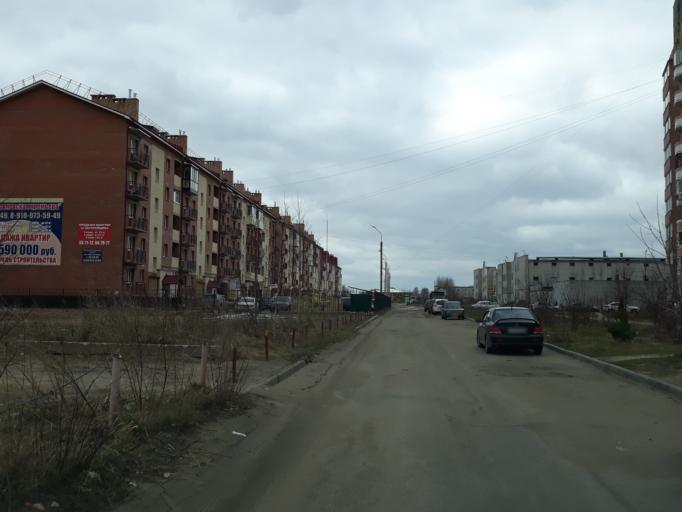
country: RU
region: Jaroslavl
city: Yaroslavl
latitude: 57.6500
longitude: 39.9682
